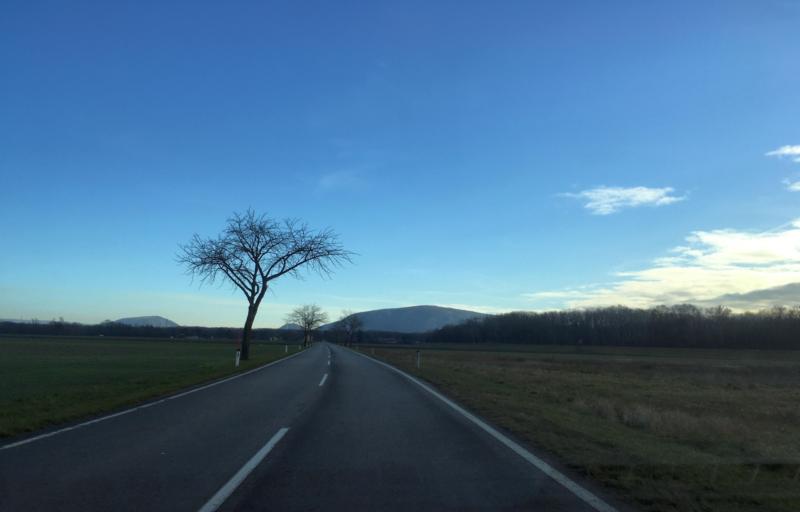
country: AT
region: Lower Austria
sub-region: Politischer Bezirk Ganserndorf
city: Engelhartstetten
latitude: 48.1507
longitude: 16.8638
